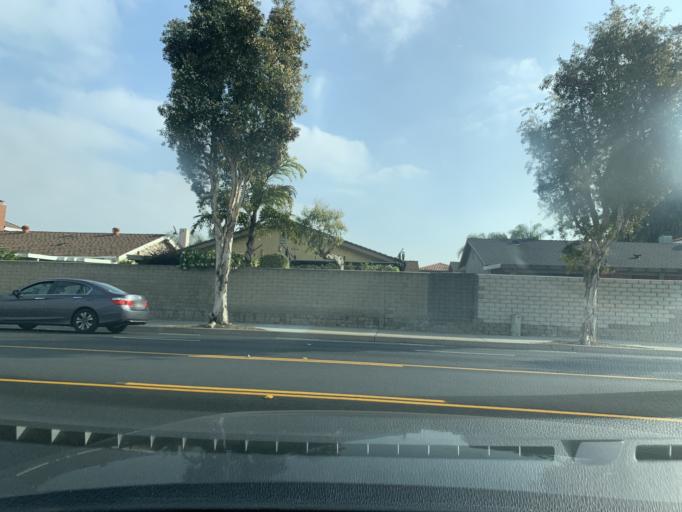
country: US
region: California
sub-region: Orange County
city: Cypress
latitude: 33.8187
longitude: -118.0369
